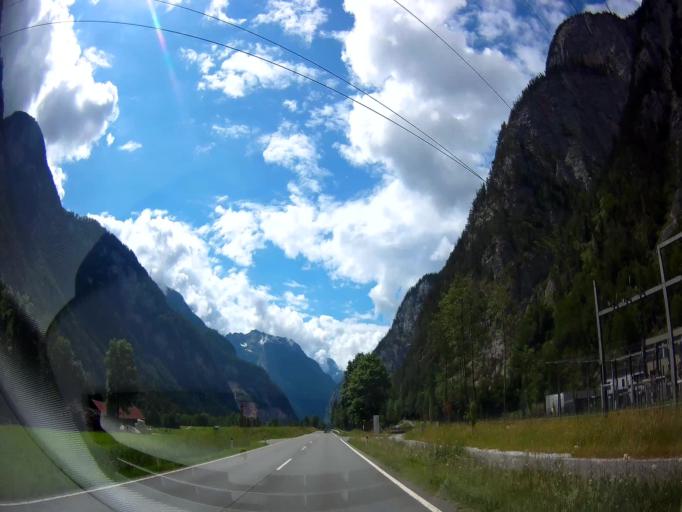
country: AT
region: Salzburg
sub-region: Politischer Bezirk Zell am See
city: Saalfelden am Steinernen Meer
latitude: 47.4903
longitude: 12.8188
